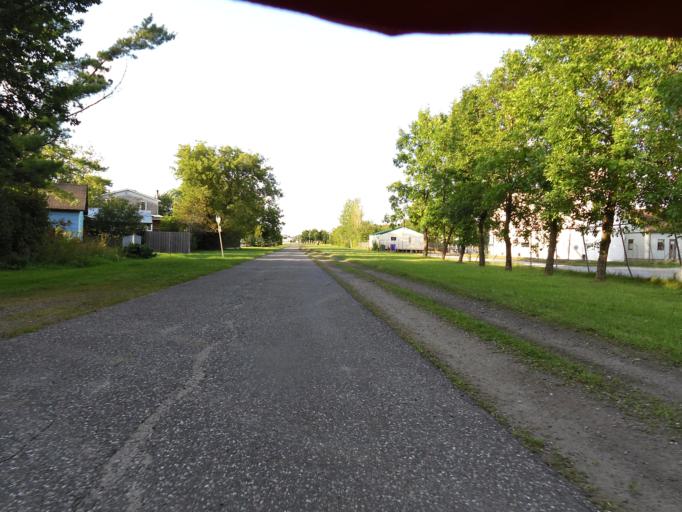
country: CA
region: Quebec
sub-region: Outaouais
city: Maniwaki
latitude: 46.3710
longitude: -75.9783
